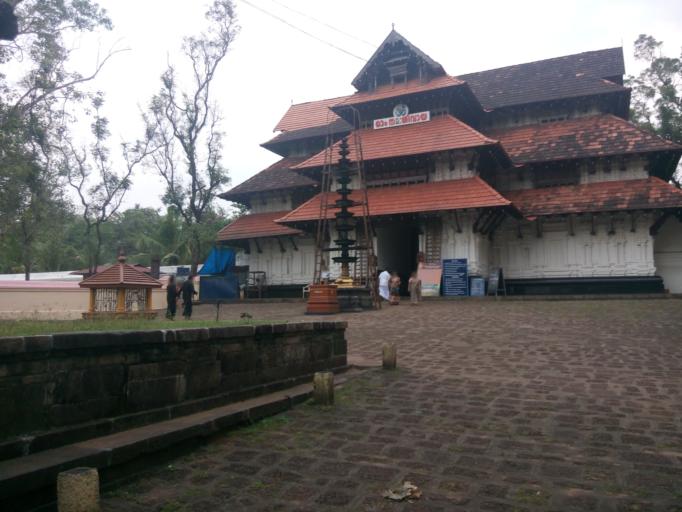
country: IN
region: Kerala
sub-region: Thrissur District
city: Trichur
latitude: 10.5241
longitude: 76.2133
